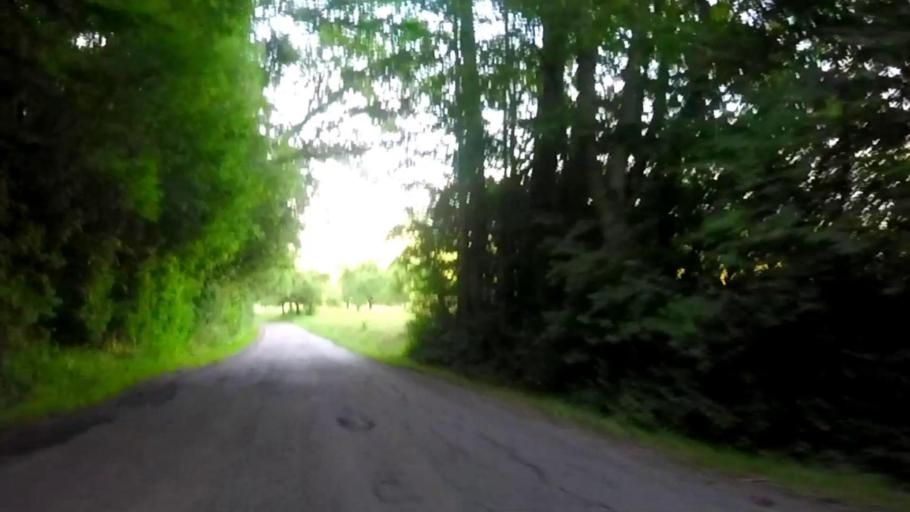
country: DE
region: Baden-Wuerttemberg
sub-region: Regierungsbezirk Stuttgart
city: Oppenweiler
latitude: 48.9733
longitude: 9.4499
